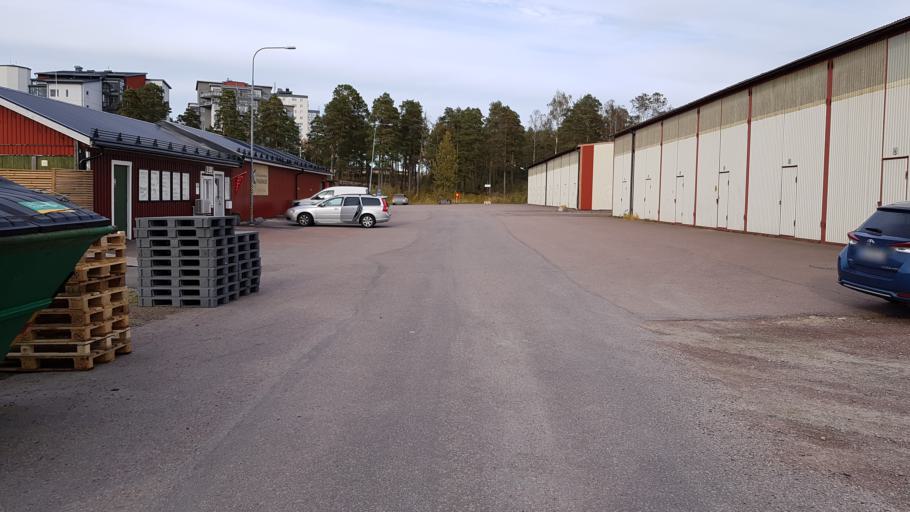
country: SE
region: Vaermland
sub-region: Hammaro Kommun
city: Skoghall
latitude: 59.3162
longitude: 13.4671
